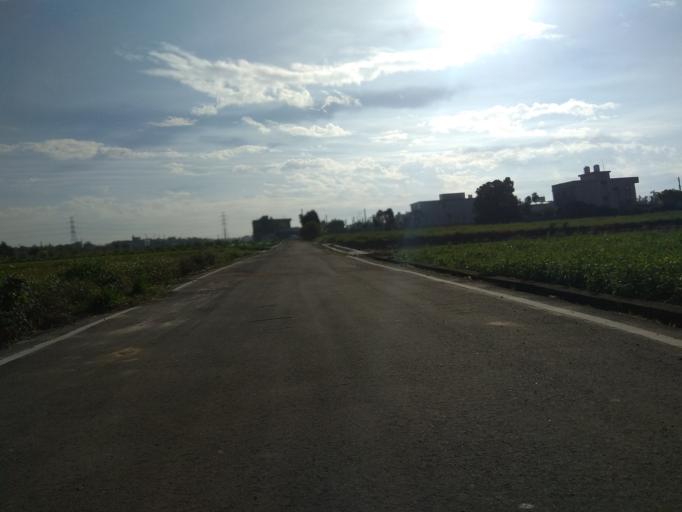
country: TW
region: Taiwan
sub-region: Hsinchu
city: Zhubei
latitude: 24.9793
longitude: 121.0597
